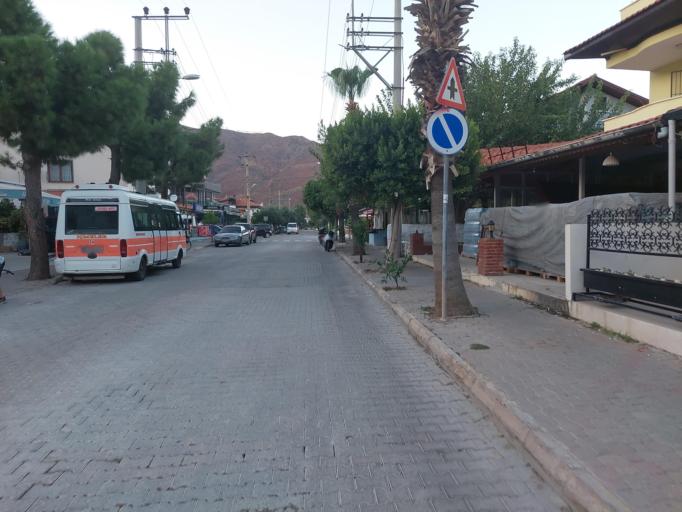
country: TR
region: Mugla
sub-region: Marmaris
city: Marmaris
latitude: 36.7960
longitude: 28.2252
